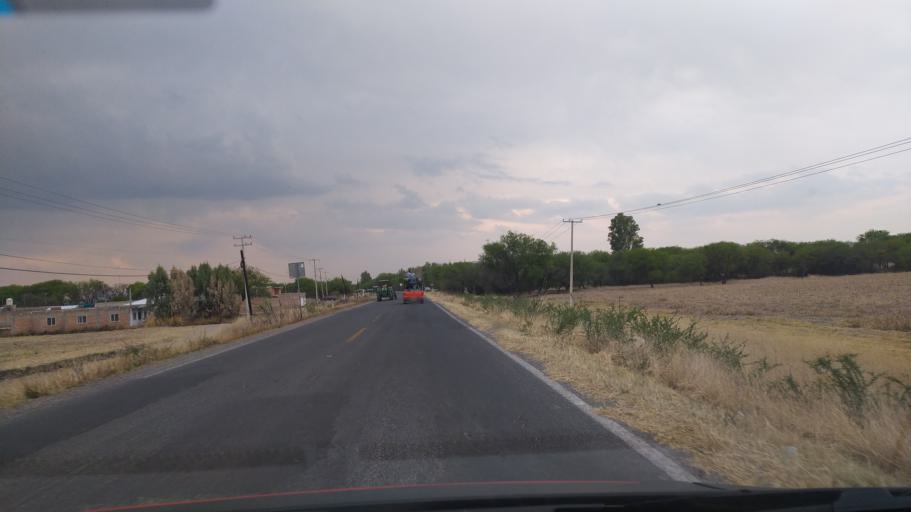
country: MX
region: Guanajuato
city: Ciudad Manuel Doblado
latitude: 20.7898
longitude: -101.9069
